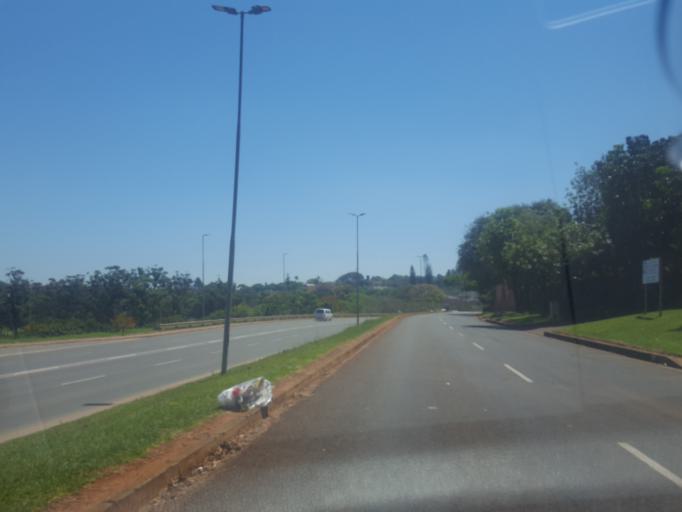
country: ZA
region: KwaZulu-Natal
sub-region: uThungulu District Municipality
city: Empangeni
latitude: -28.7575
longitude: 31.9002
